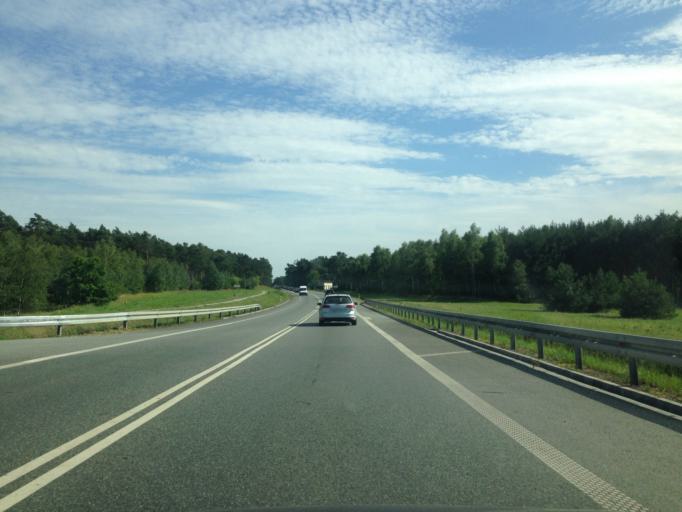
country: PL
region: Kujawsko-Pomorskie
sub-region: Powiat torunski
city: Lubicz Dolny
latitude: 52.9680
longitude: 18.6822
